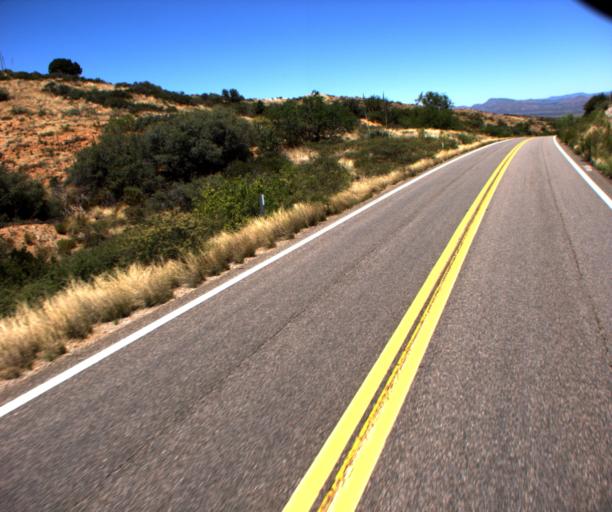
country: US
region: Arizona
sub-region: Gila County
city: Globe
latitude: 33.2991
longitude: -110.7462
